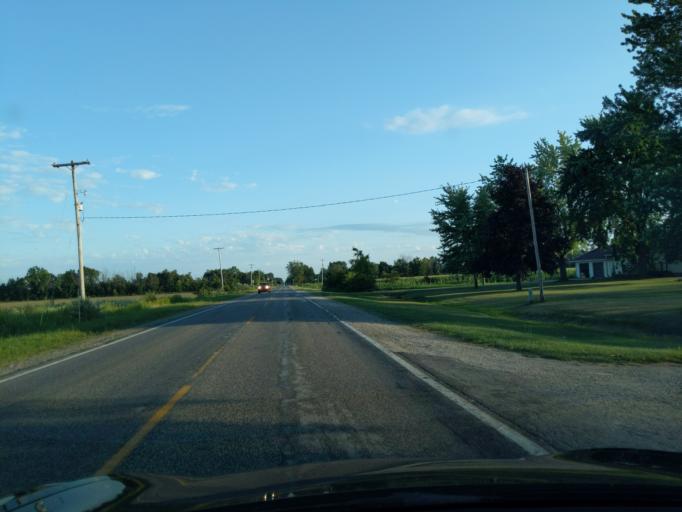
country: US
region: Michigan
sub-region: Gratiot County
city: Breckenridge
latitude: 43.4151
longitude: -84.3699
